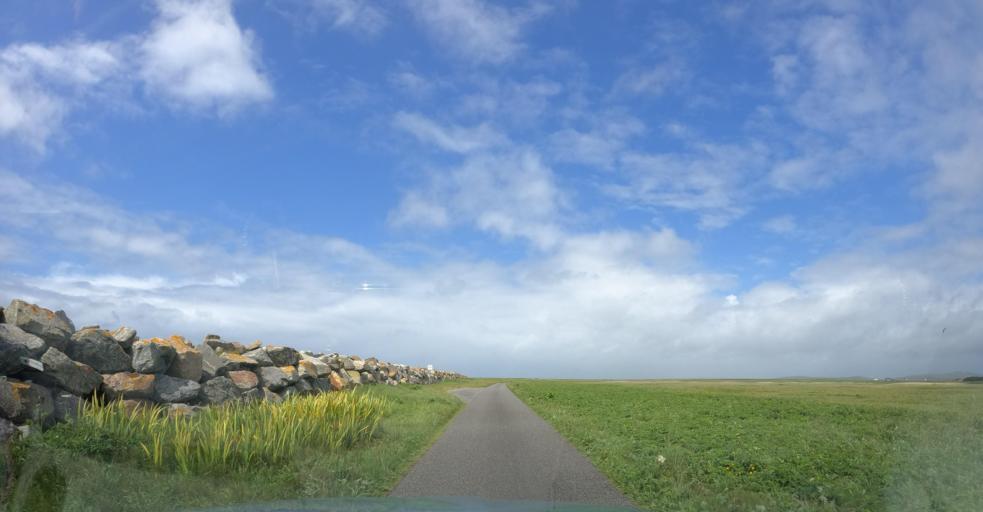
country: GB
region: Scotland
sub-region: Eilean Siar
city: Isle of South Uist
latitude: 57.2819
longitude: -7.4193
